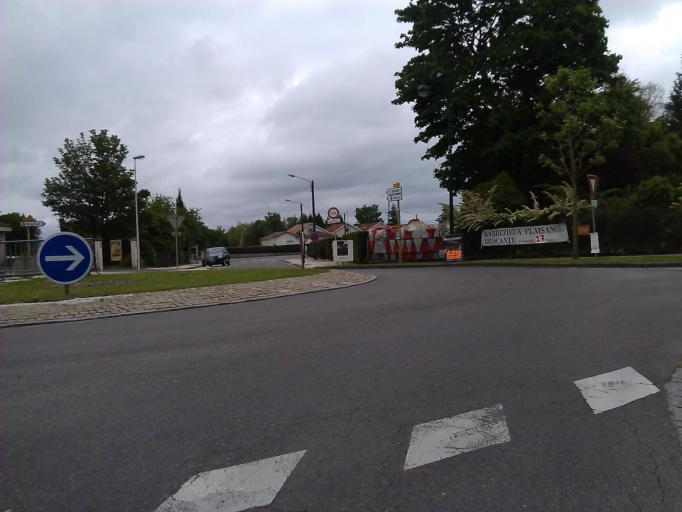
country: FR
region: Poitou-Charentes
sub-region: Departement de la Charente
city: Barbezieux-Saint-Hilaire
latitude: 45.4770
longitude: -0.1483
